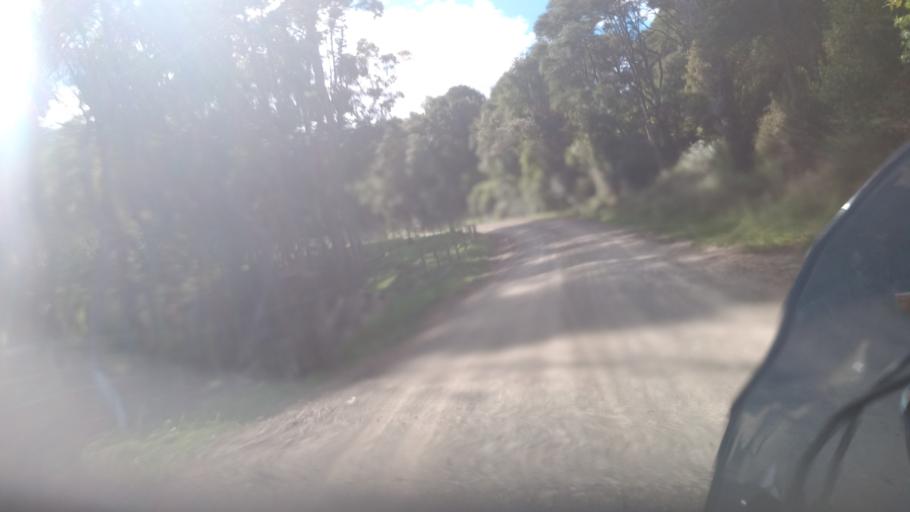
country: NZ
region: Gisborne
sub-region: Gisborne District
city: Gisborne
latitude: -38.4023
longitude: 177.6800
